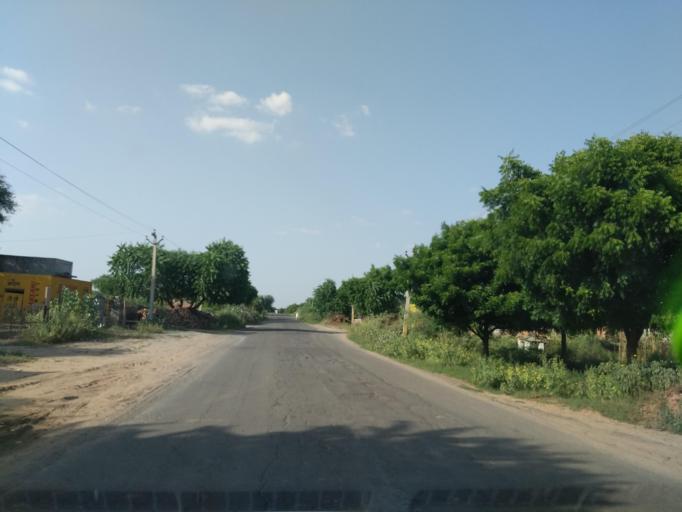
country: IN
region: Rajasthan
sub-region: Churu
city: Rajgarh
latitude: 28.5145
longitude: 75.3832
